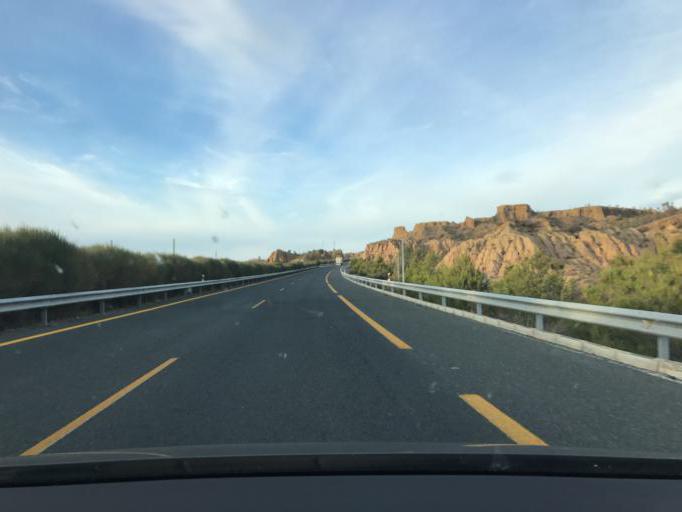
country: ES
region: Andalusia
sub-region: Provincia de Granada
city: Guadix
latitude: 37.3074
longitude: -3.1121
